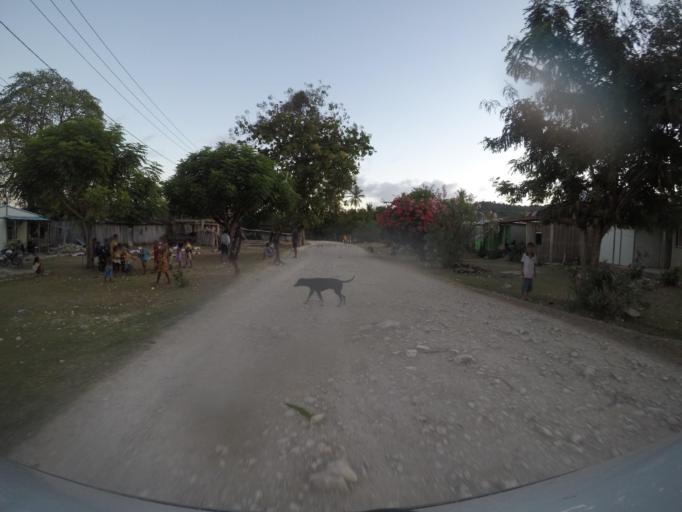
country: TL
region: Viqueque
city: Viqueque
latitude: -8.7772
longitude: 126.6370
